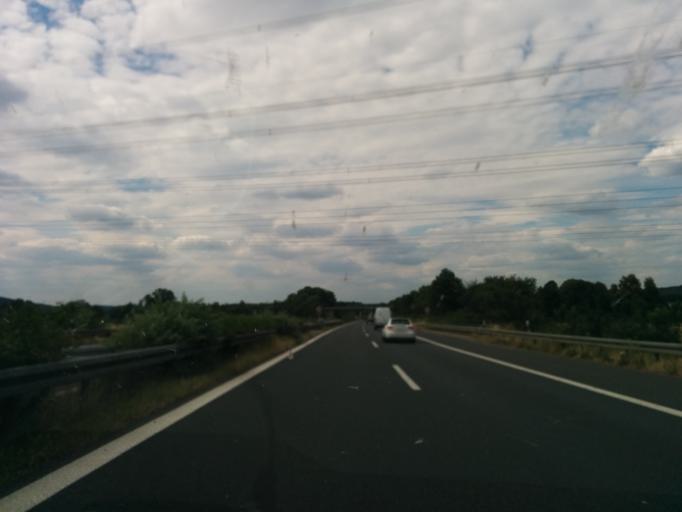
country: DE
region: Bavaria
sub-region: Upper Franconia
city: Gundelsheim
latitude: 49.9327
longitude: 10.9129
